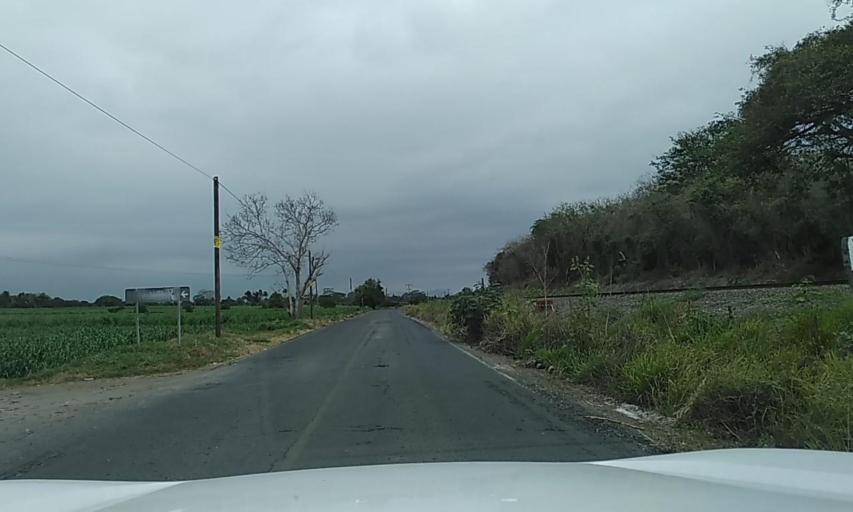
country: MX
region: Veracruz
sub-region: La Antigua
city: Nicolas Blanco (San Pancho)
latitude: 19.3033
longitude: -96.3156
